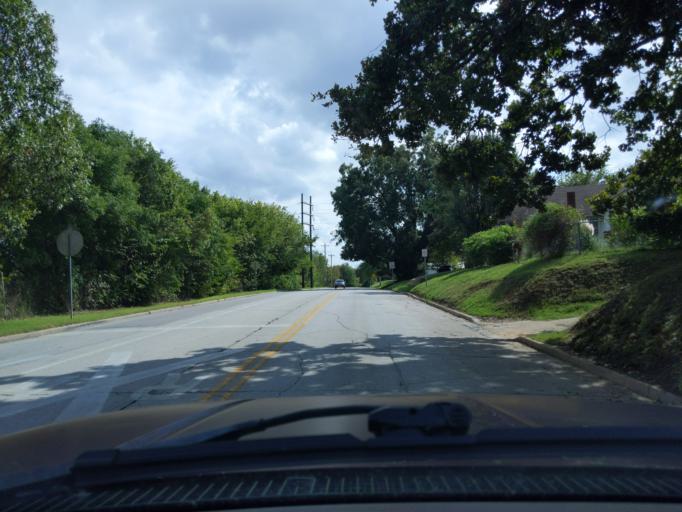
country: US
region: Oklahoma
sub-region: Tulsa County
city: Tulsa
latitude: 36.1097
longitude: -96.0123
